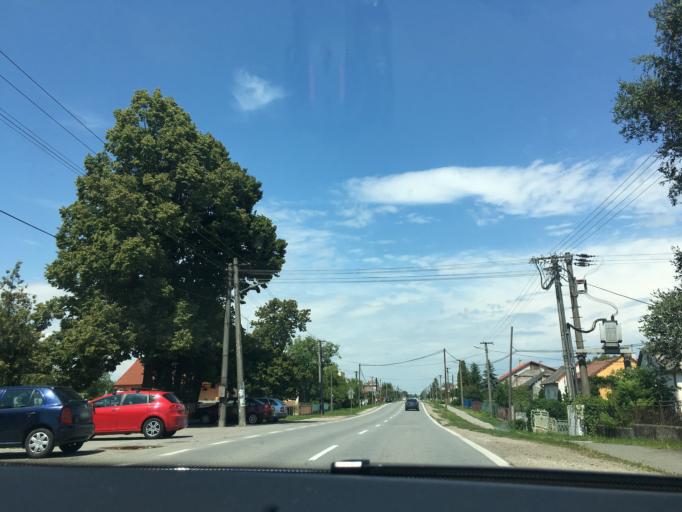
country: SK
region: Kosicky
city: Secovce
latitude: 48.7888
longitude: 21.6810
